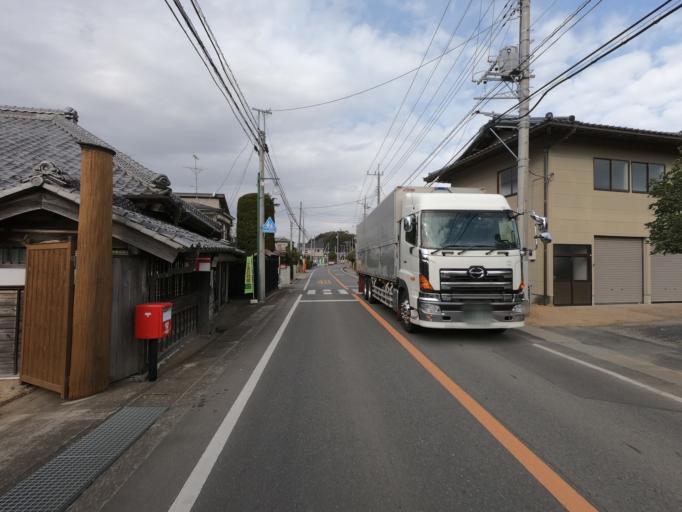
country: JP
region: Ibaraki
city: Inashiki
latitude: 36.0892
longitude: 140.4248
